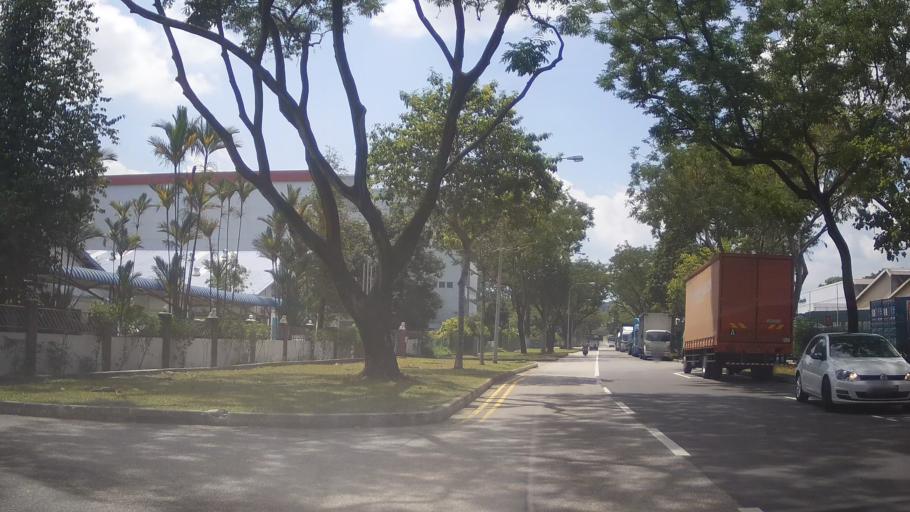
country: MY
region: Johor
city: Johor Bahru
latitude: 1.3313
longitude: 103.7124
